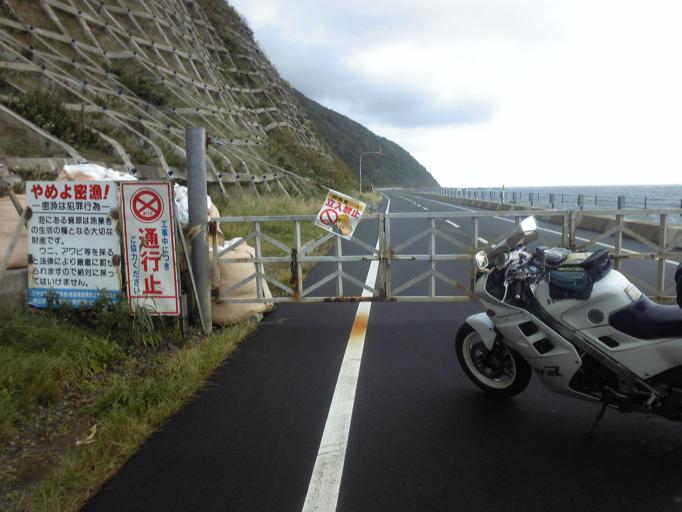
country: JP
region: Hokkaido
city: Iwanai
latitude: 42.3414
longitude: 139.7767
